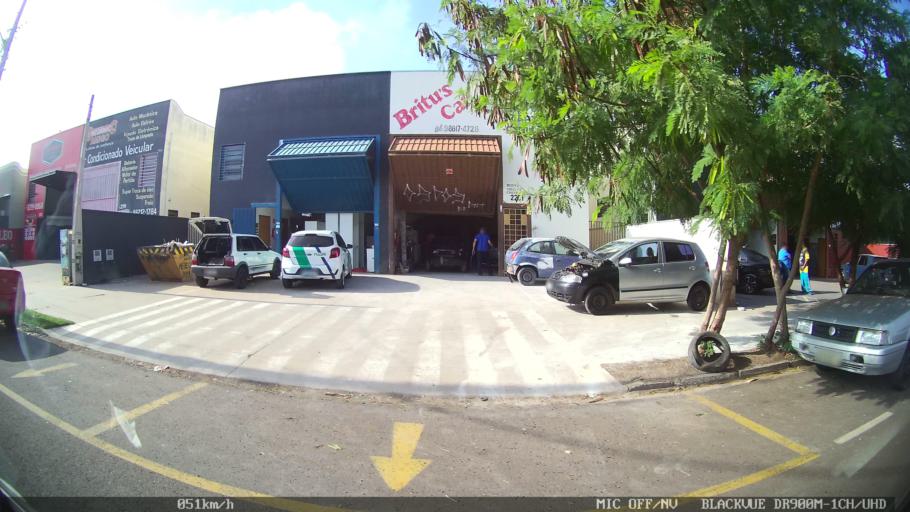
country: BR
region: Sao Paulo
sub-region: Sao Jose Do Rio Preto
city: Sao Jose do Rio Preto
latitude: -20.7997
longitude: -49.4304
